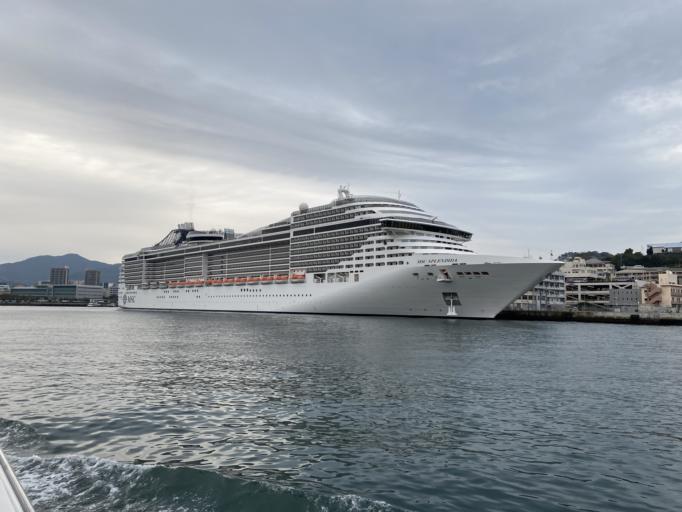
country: JP
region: Nagasaki
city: Nagasaki-shi
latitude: 32.7357
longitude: 129.8642
